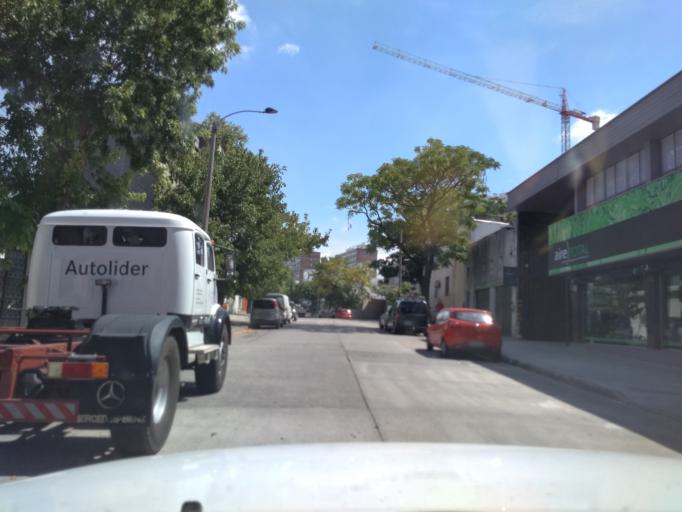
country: UY
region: Montevideo
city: Montevideo
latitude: -34.8792
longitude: -56.1973
